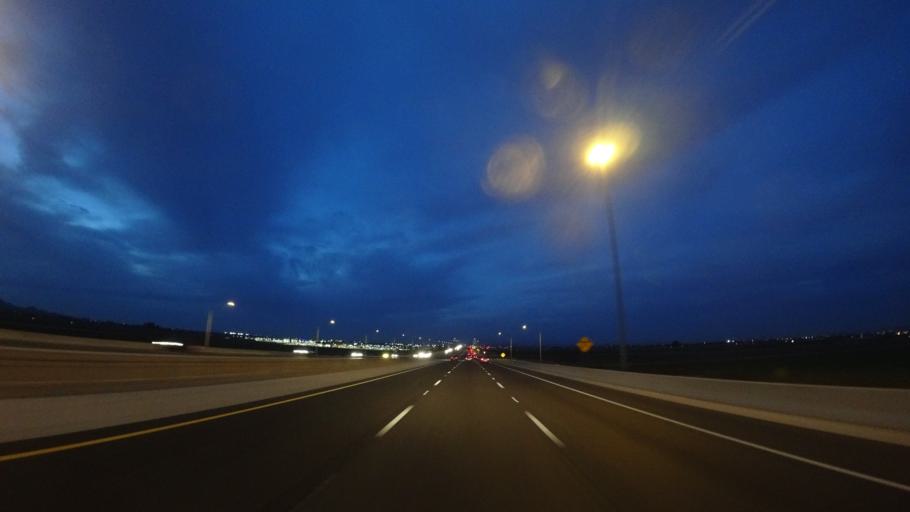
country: US
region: Arizona
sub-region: Maricopa County
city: Citrus Park
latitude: 33.5966
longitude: -112.4180
